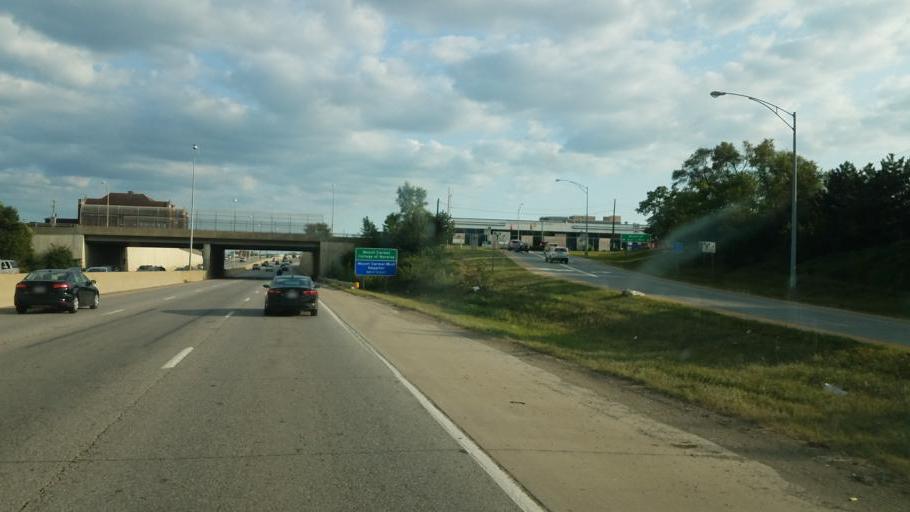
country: US
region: Ohio
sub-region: Franklin County
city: Columbus
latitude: 39.9611
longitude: -83.0191
